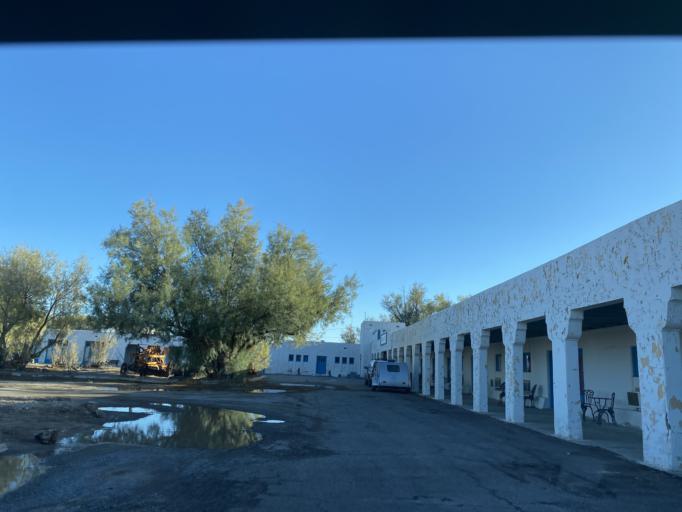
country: US
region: Nevada
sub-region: Nye County
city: Pahrump
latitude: 36.3014
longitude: -116.4150
